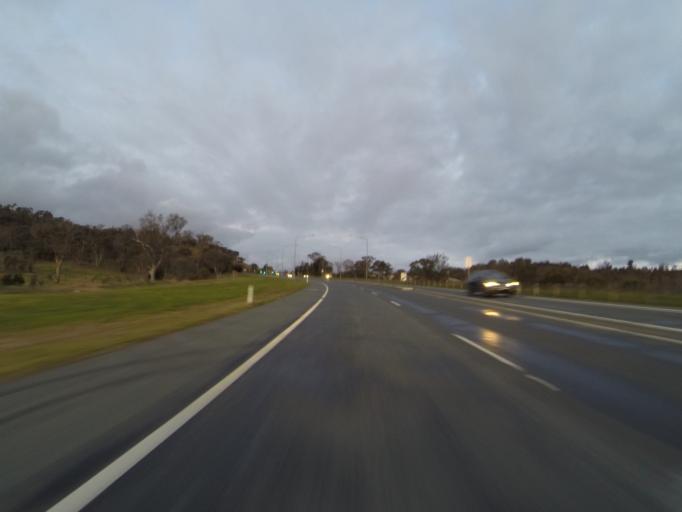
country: AU
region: Australian Capital Territory
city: Kaleen
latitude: -35.2132
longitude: 149.1802
